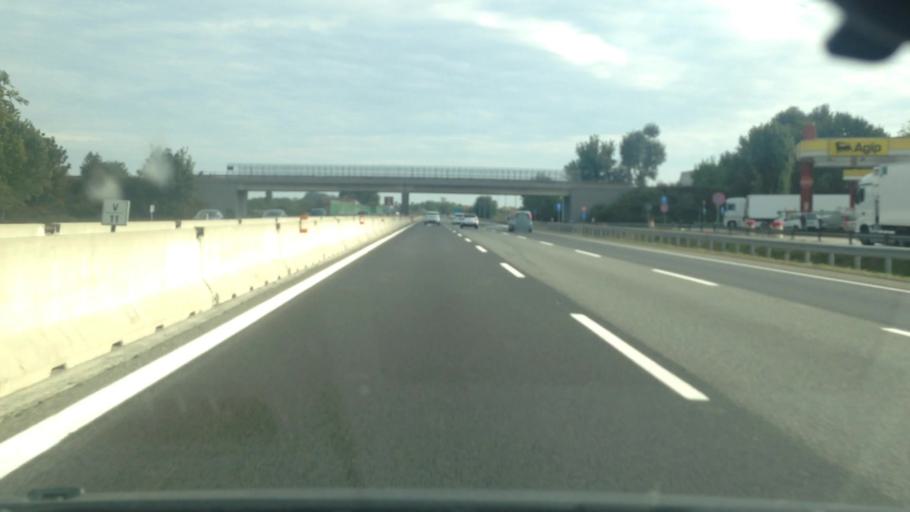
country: IT
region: Piedmont
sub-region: Provincia di Torino
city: Nichelino
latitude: 44.9818
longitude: 7.6451
